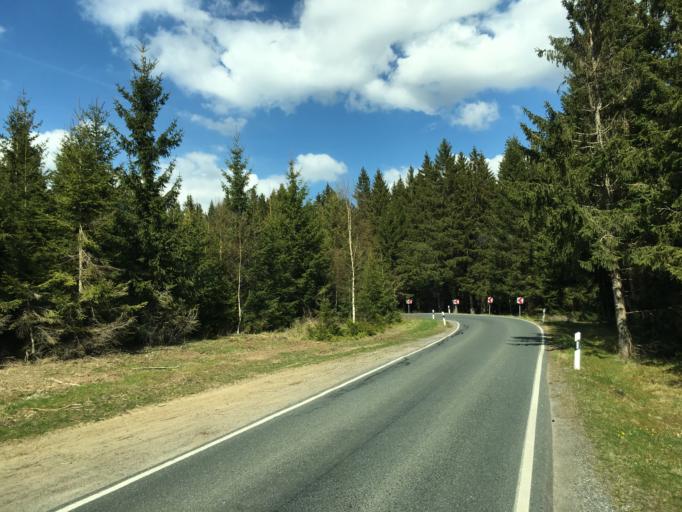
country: DE
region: Saxony-Anhalt
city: Benneckenstein
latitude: 51.7012
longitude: 10.6882
